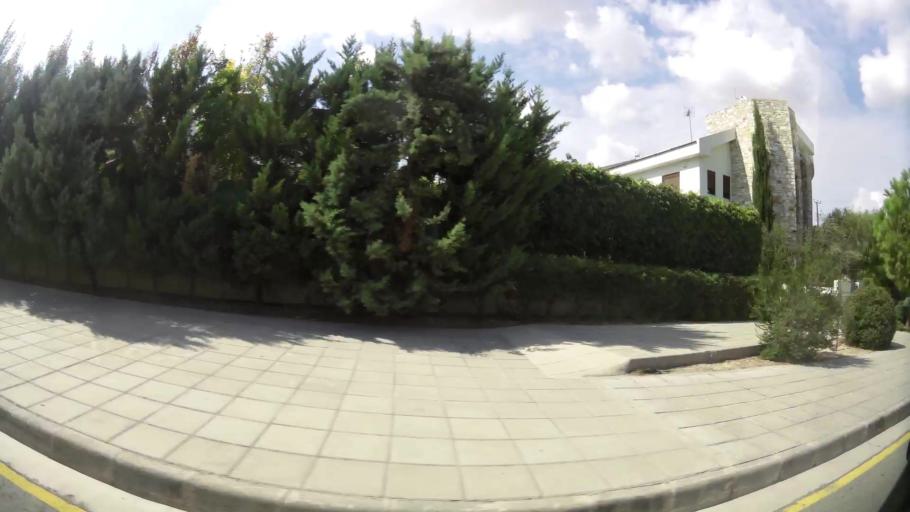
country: CY
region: Larnaka
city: Aradippou
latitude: 34.9536
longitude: 33.5676
